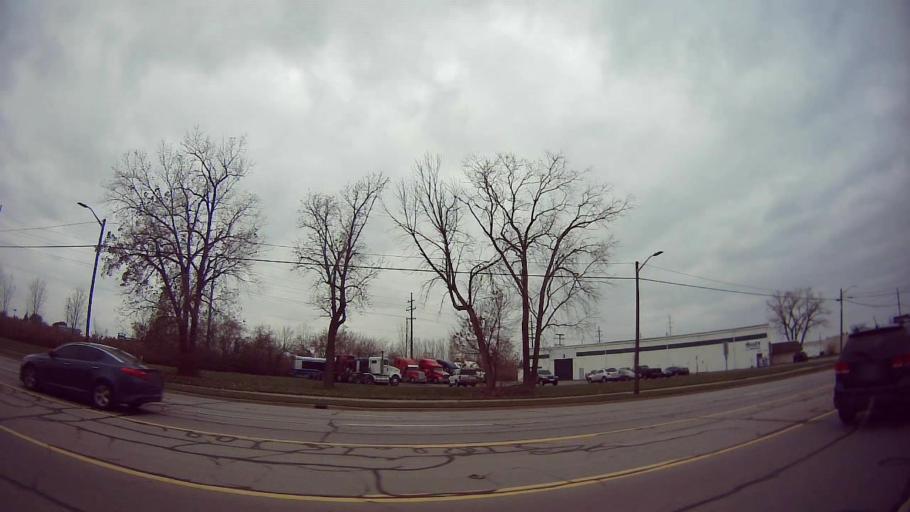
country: US
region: Michigan
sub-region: Macomb County
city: Eastpointe
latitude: 42.4839
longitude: -82.9765
